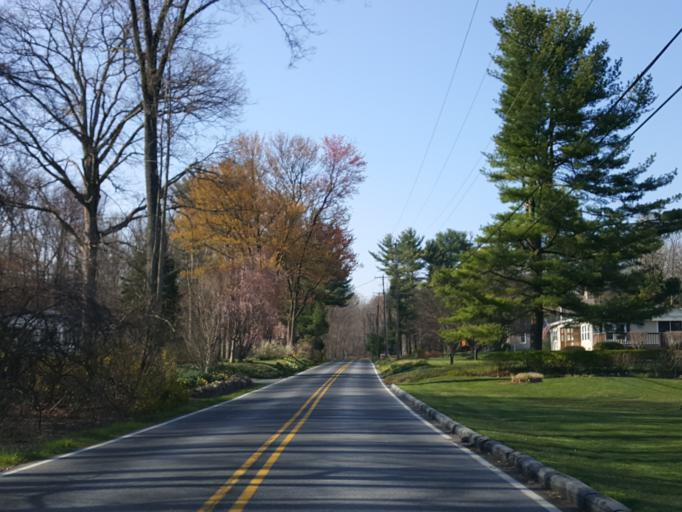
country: US
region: Pennsylvania
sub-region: Lebanon County
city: Campbelltown
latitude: 40.2531
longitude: -76.5146
